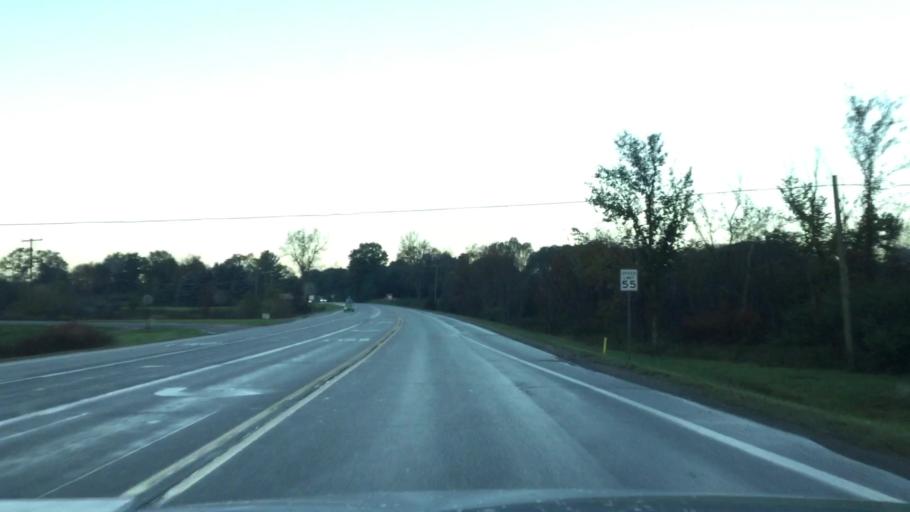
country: US
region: Michigan
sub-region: Livingston County
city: Howell
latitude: 42.6295
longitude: -83.8757
